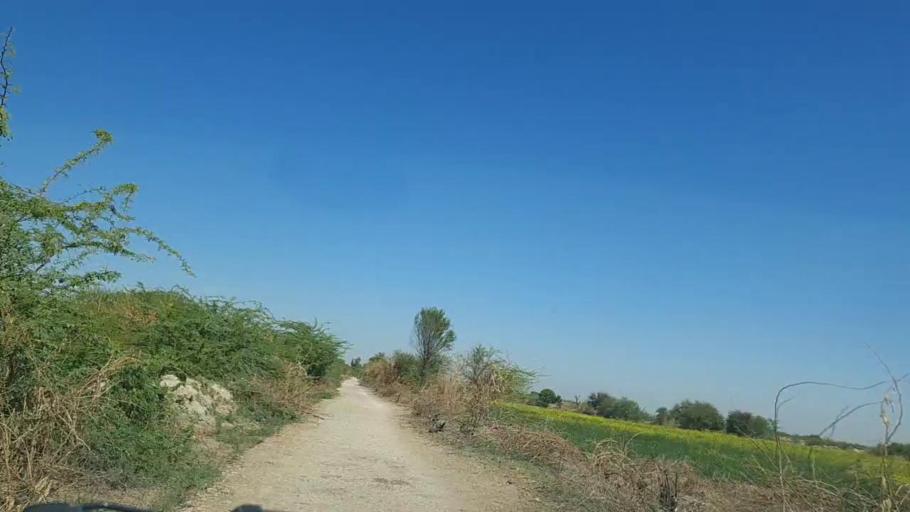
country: PK
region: Sindh
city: Dhoro Naro
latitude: 25.4717
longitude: 69.5127
